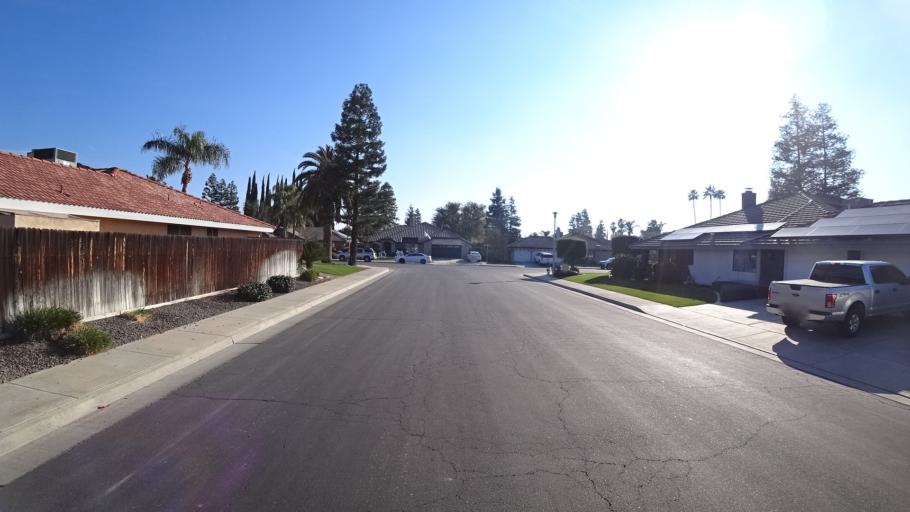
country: US
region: California
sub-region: Kern County
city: Greenacres
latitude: 35.3271
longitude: -119.1000
